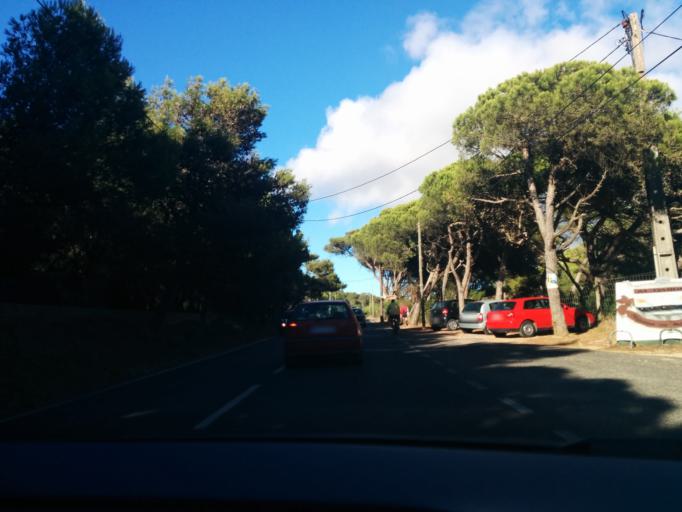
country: PT
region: Lisbon
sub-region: Cascais
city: Cascais
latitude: 38.7325
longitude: -9.4675
